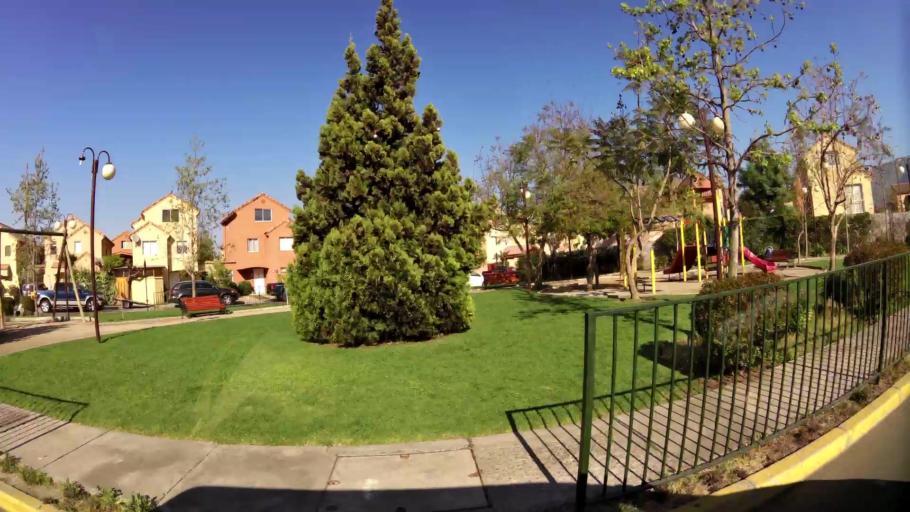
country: CL
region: Santiago Metropolitan
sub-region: Provincia de Chacabuco
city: Chicureo Abajo
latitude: -33.3530
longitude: -70.6644
